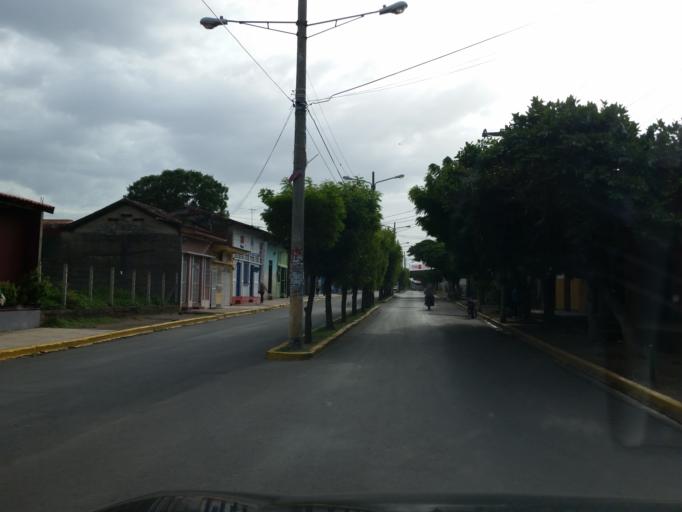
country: NI
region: Granada
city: Granada
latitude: 11.9368
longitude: -85.9563
